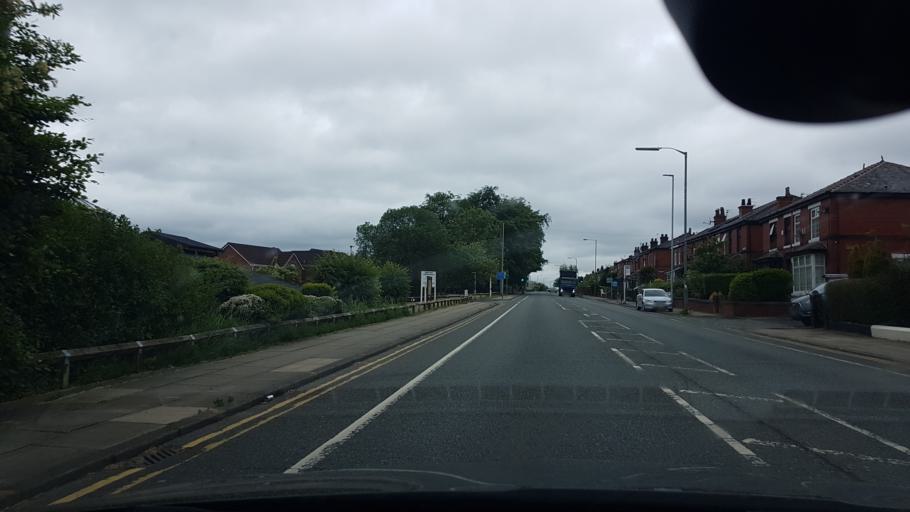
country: GB
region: England
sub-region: Borough of Bury
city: Radcliffe
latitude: 53.5872
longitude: -2.3227
